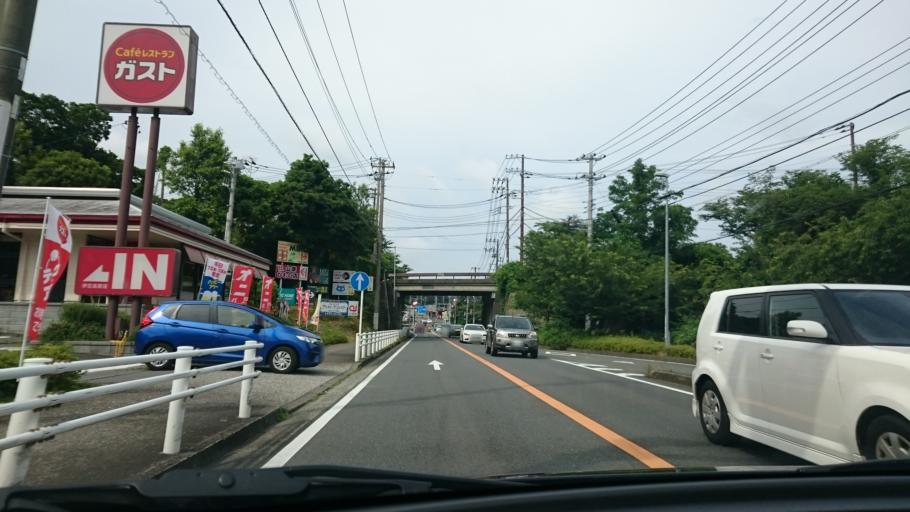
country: JP
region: Shizuoka
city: Ito
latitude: 34.8805
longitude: 139.1067
